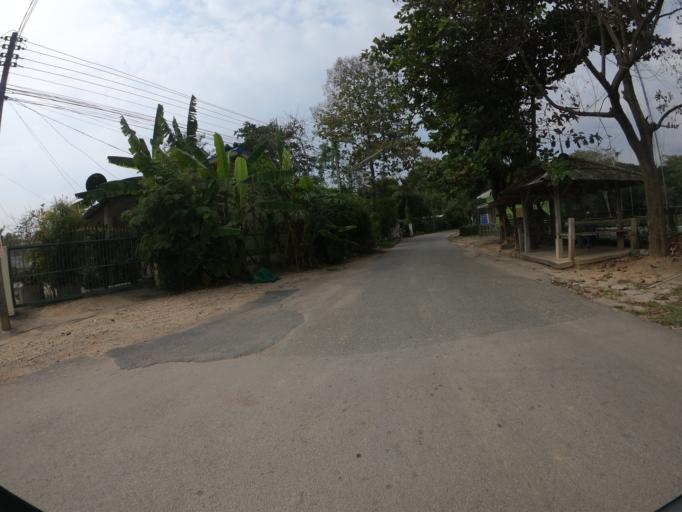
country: TH
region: Chiang Mai
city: Hang Dong
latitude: 18.7375
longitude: 98.9260
